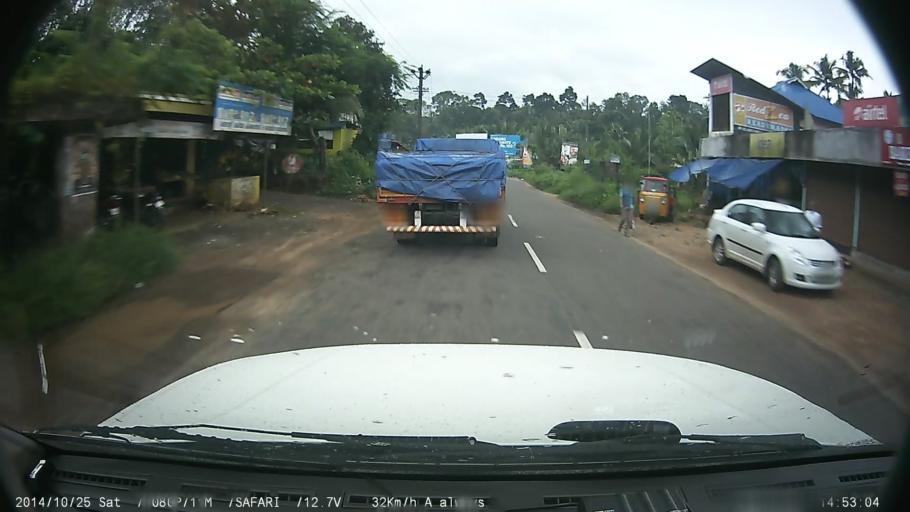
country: IN
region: Kerala
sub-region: Ernakulam
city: Piravam
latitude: 9.8881
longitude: 76.5907
